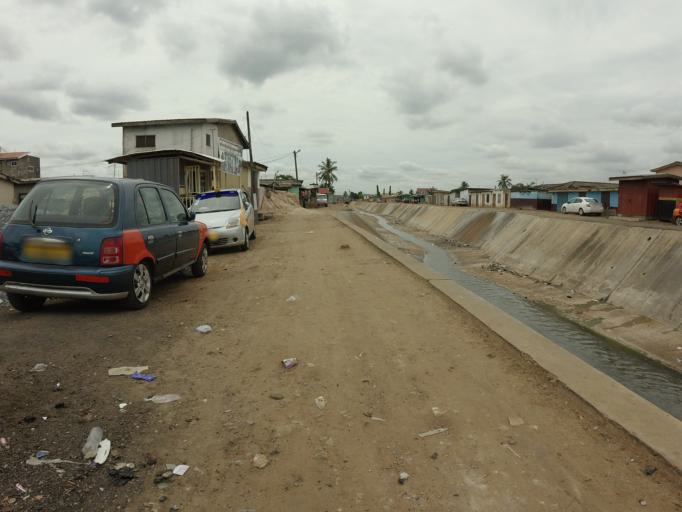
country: GH
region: Greater Accra
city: Accra
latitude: 5.5947
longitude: -0.2132
